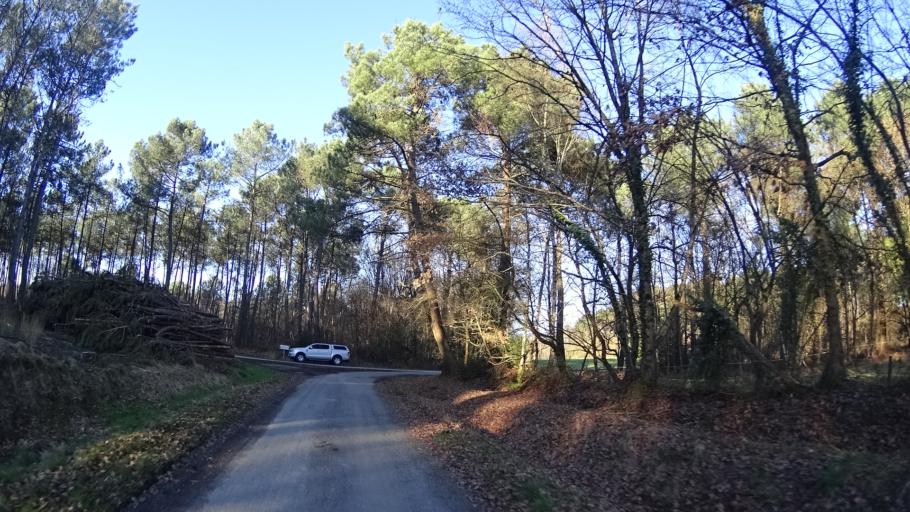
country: FR
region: Brittany
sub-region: Departement du Morbihan
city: Saint-Jacut-les-Pins
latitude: 47.6773
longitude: -2.1830
